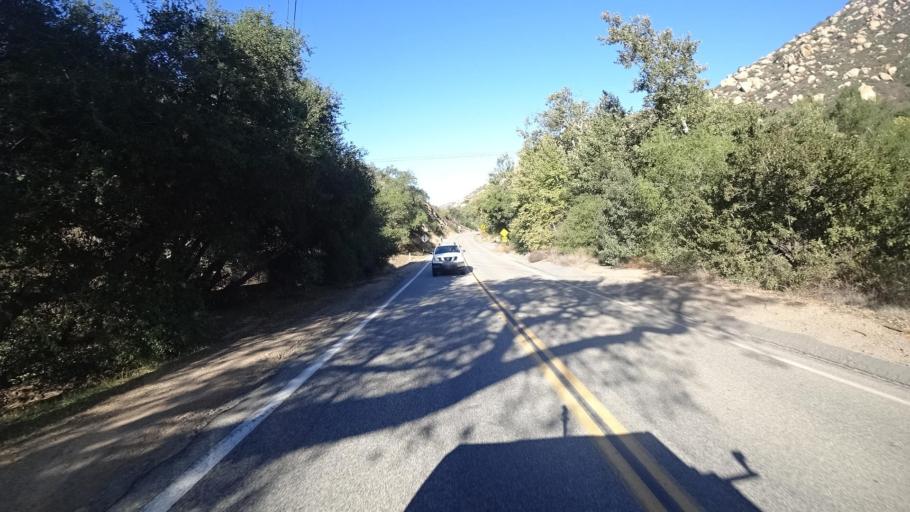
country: US
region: California
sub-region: San Diego County
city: Jamul
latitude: 32.6718
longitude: -116.7631
